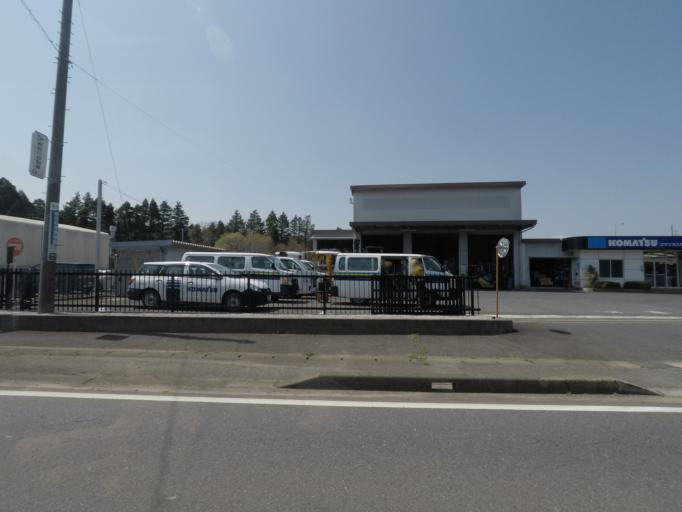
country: JP
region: Chiba
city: Naruto
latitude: 35.6667
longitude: 140.4383
